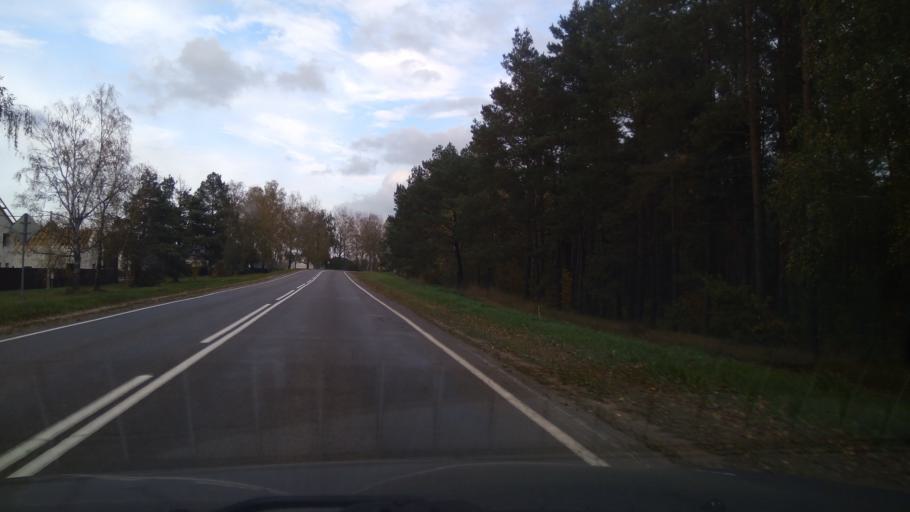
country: BY
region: Minsk
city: Svislach
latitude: 53.6523
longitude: 27.9308
